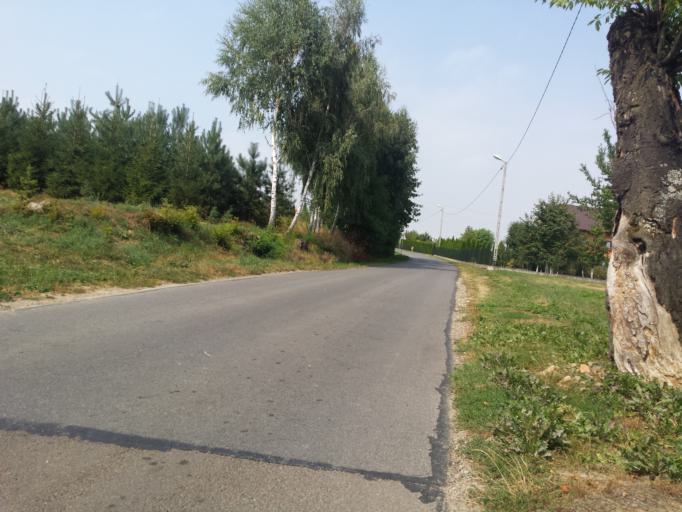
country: PL
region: Subcarpathian Voivodeship
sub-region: Powiat rzeszowski
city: Dynow
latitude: 49.8188
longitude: 22.2091
